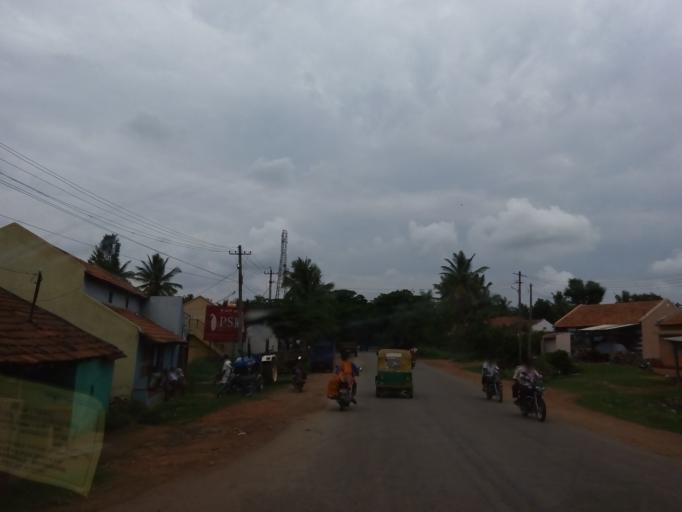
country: IN
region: Karnataka
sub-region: Hassan
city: Channarayapatna
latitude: 12.8825
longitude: 76.4165
